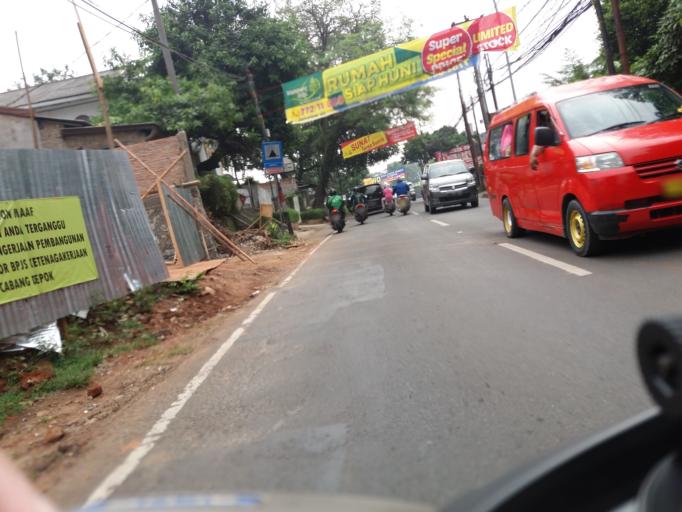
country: ID
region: West Java
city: Depok
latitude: -6.4008
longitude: 106.8282
